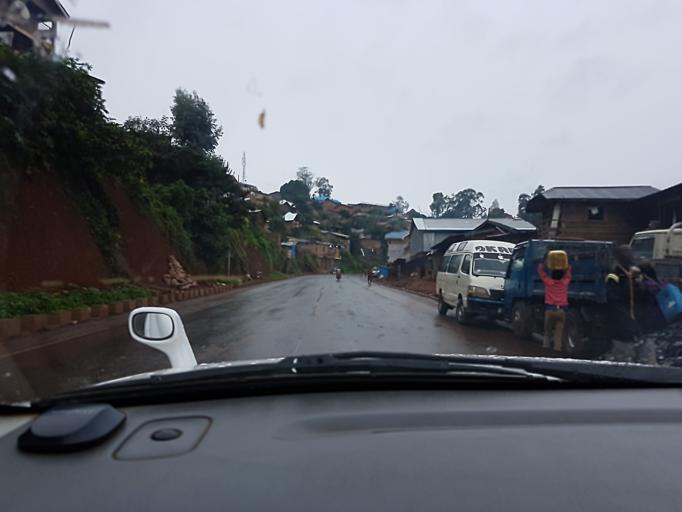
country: CD
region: South Kivu
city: Bukavu
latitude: -2.5152
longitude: 28.8565
